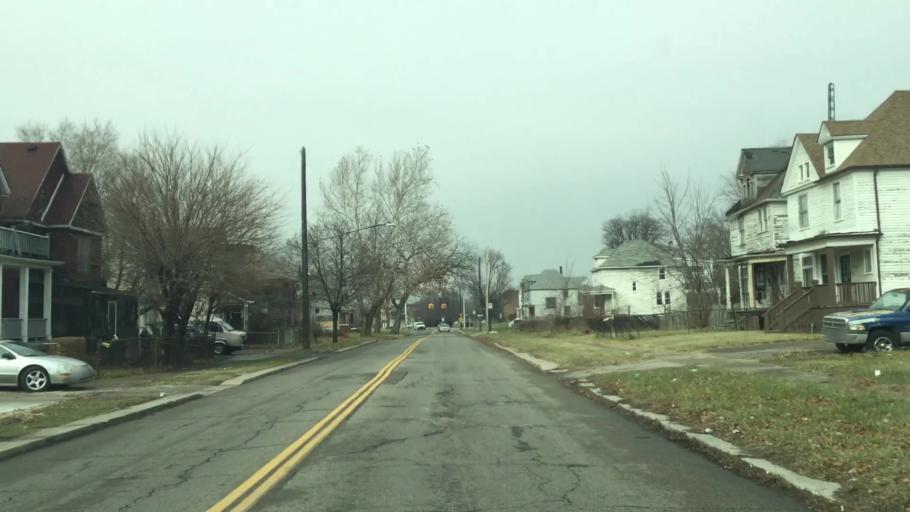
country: US
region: Michigan
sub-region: Wayne County
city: Highland Park
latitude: 42.3542
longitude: -83.0951
